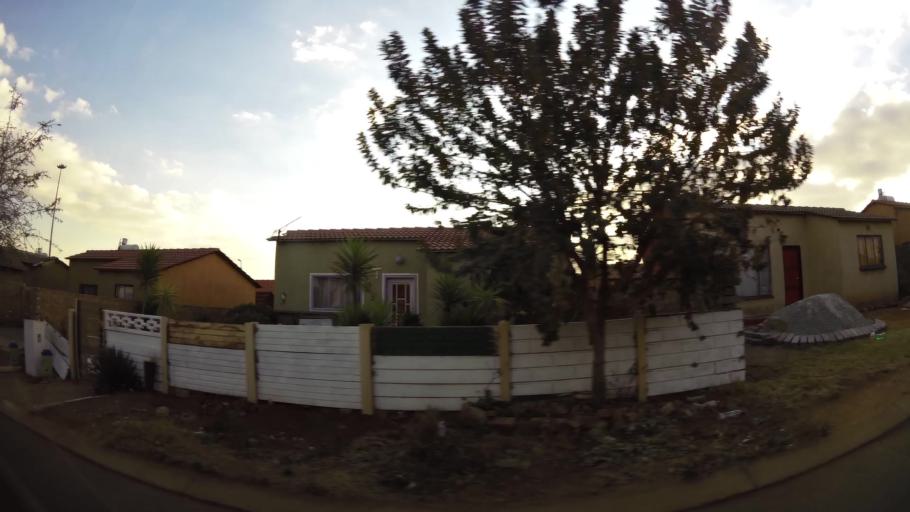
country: ZA
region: Gauteng
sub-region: West Rand District Municipality
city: Krugersdorp
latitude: -26.0777
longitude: 27.7598
